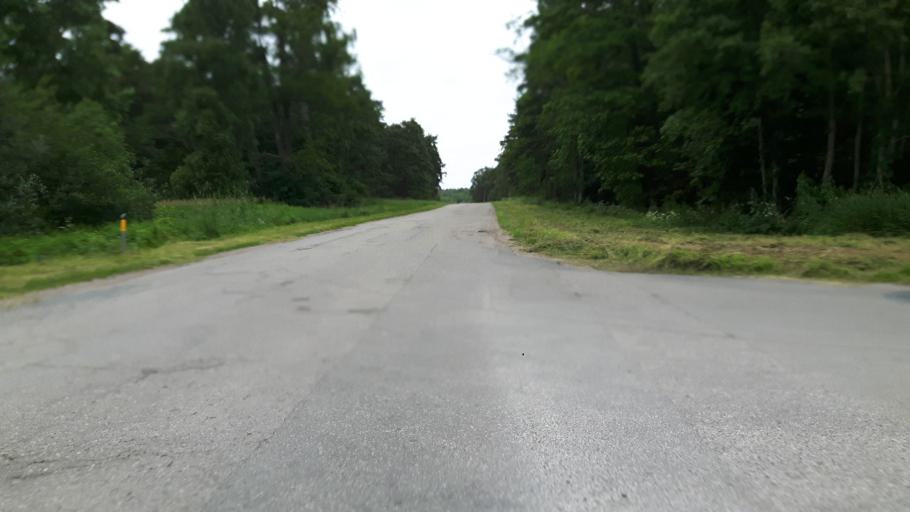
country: LV
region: Liepaja
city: Vec-Liepaja
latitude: 56.5848
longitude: 21.0269
